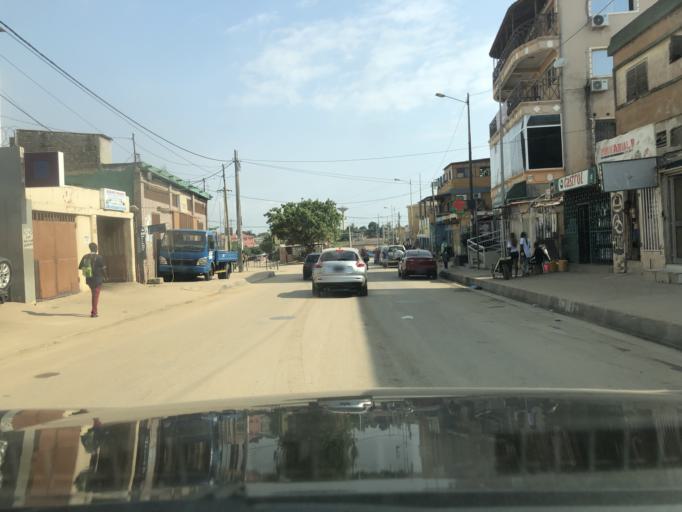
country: AO
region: Luanda
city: Luanda
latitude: -8.8495
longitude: 13.2582
